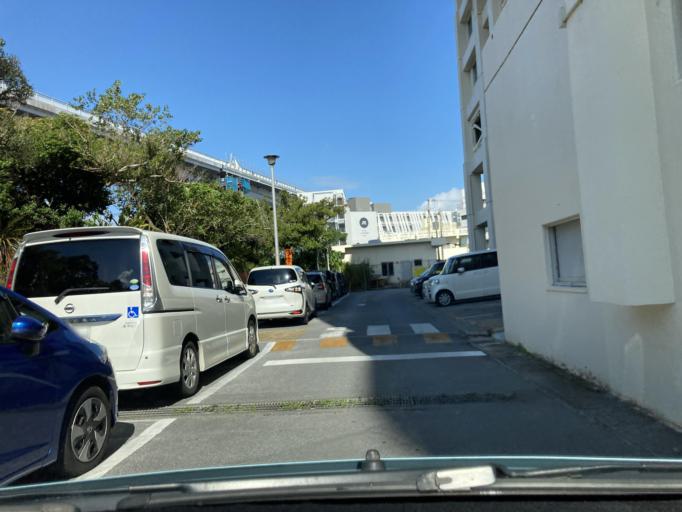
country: JP
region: Okinawa
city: Naha-shi
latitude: 26.2246
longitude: 127.6778
